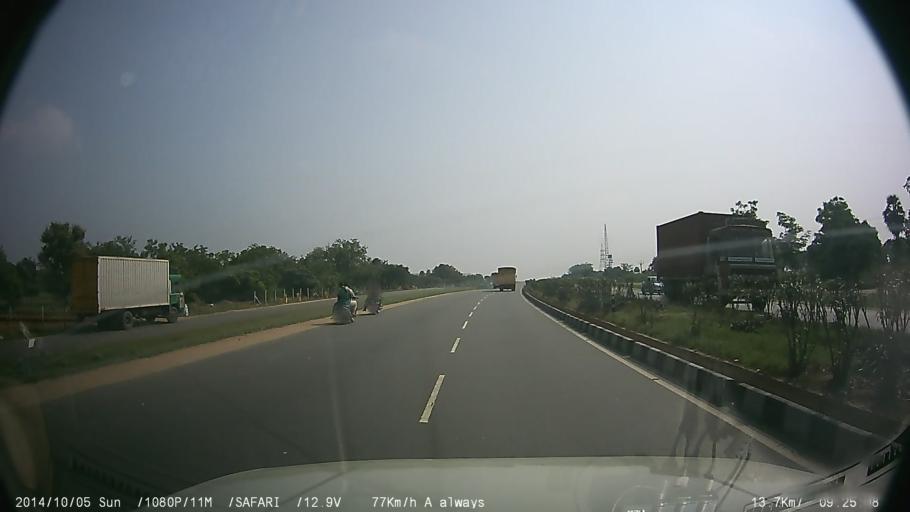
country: IN
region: Tamil Nadu
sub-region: Erode
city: Perundurai
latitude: 11.3148
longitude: 77.6136
